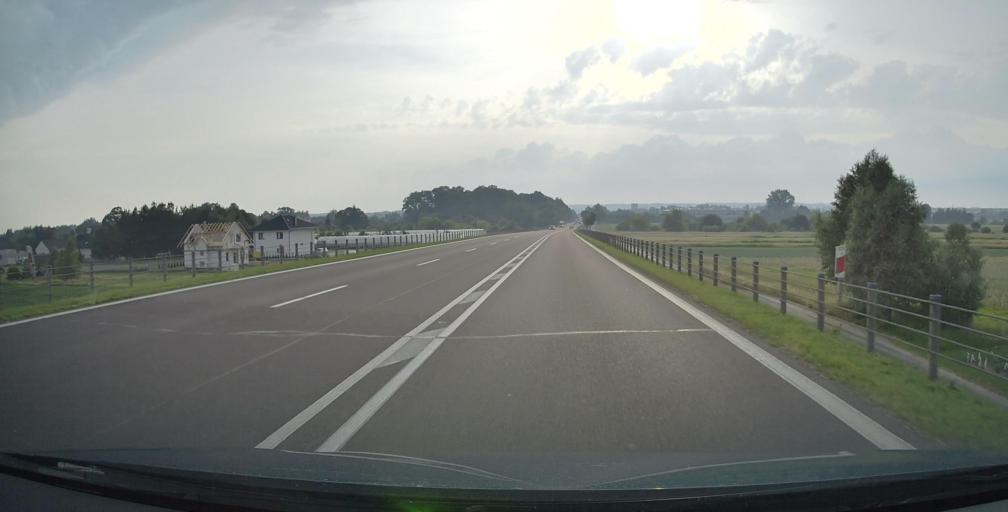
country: PL
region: Masovian Voivodeship
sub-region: Siedlce
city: Siedlce
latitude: 52.1319
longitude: 22.3038
